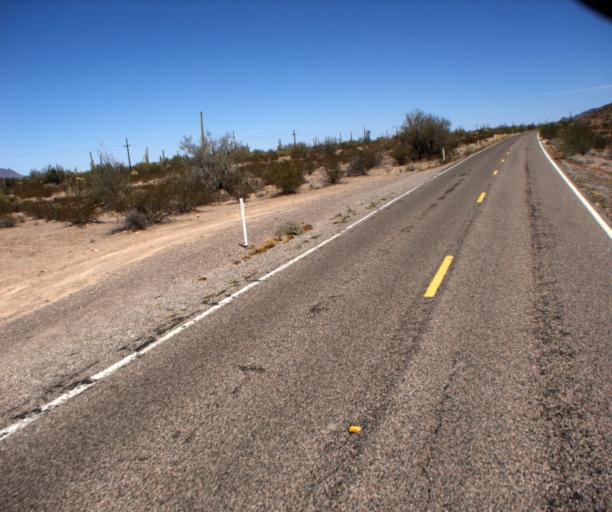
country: US
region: Arizona
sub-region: Pima County
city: Ajo
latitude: 32.2214
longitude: -112.7567
